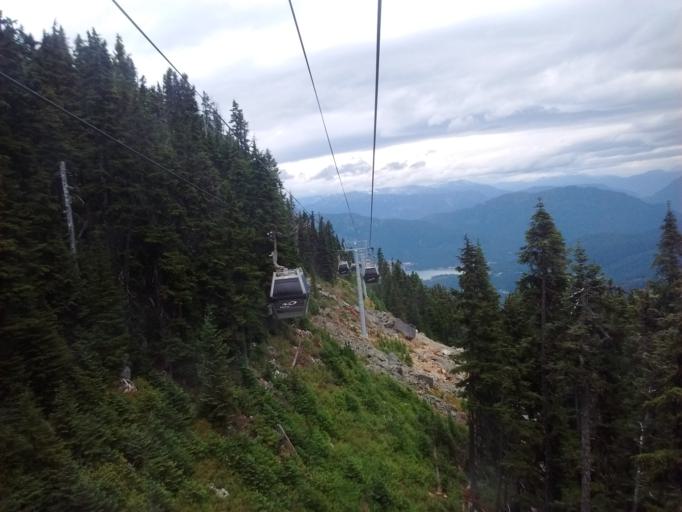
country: CA
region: British Columbia
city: Whistler
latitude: 50.0802
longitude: -122.9486
